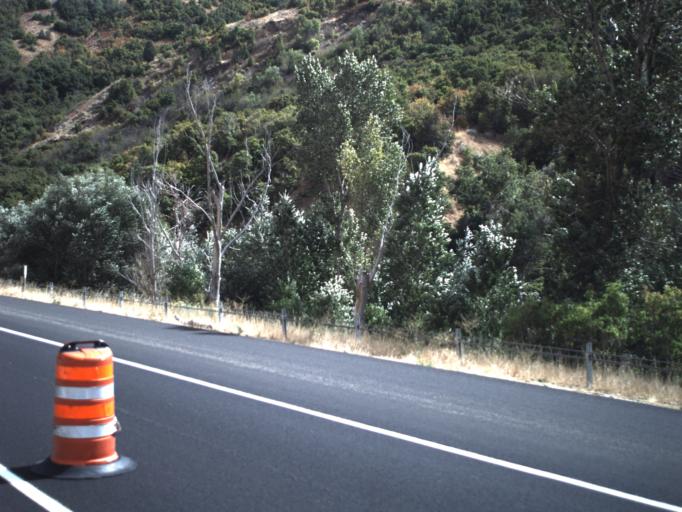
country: US
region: Utah
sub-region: Box Elder County
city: Brigham City
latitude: 41.4981
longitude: -111.9780
